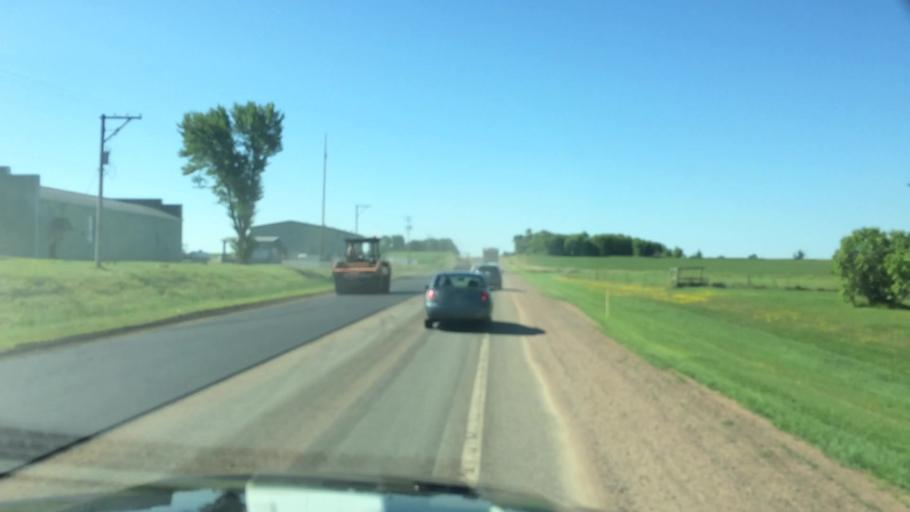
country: US
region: Wisconsin
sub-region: Marathon County
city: Stratford
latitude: 44.8935
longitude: -90.0789
